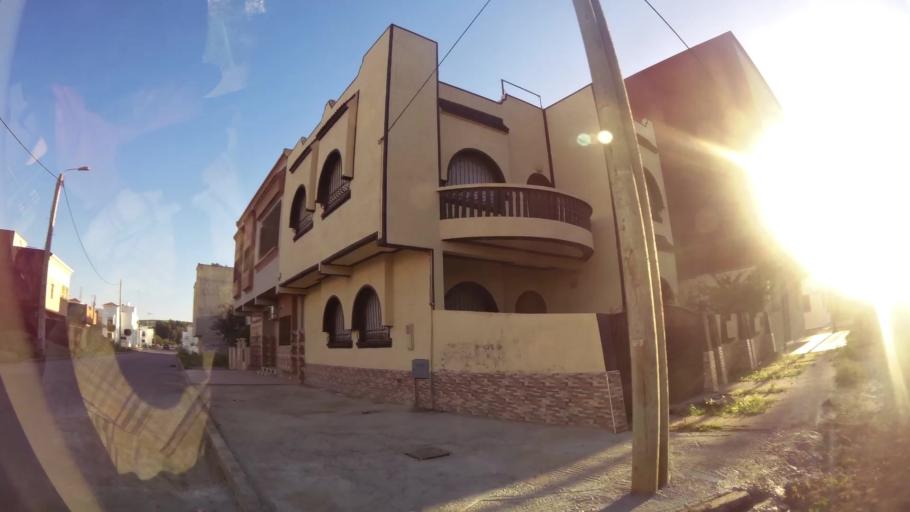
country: MA
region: Oriental
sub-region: Berkane-Taourirt
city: Madagh
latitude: 35.0821
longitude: -2.2397
